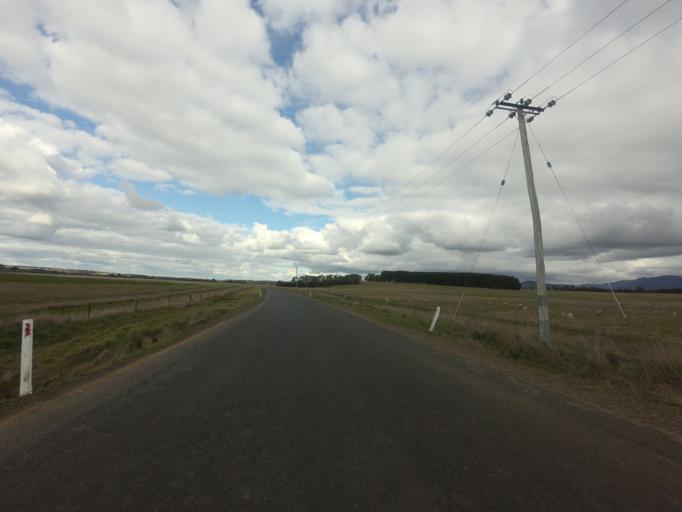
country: AU
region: Tasmania
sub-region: Northern Midlands
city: Longford
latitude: -41.7741
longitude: 147.0912
